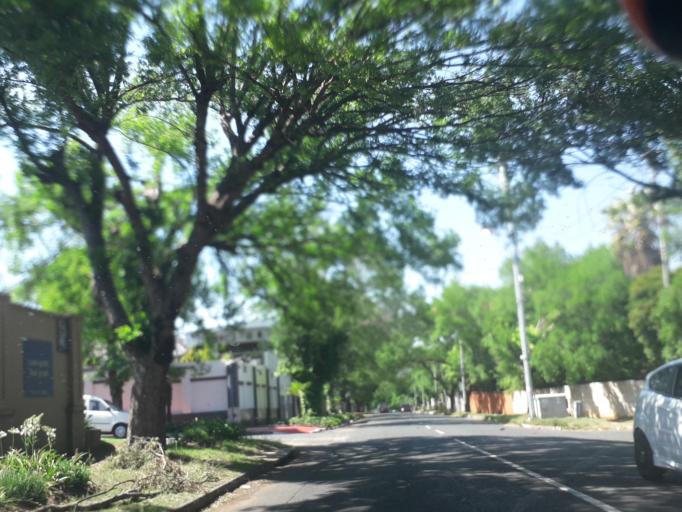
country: ZA
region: Gauteng
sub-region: City of Johannesburg Metropolitan Municipality
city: Johannesburg
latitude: -26.1434
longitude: 28.0767
